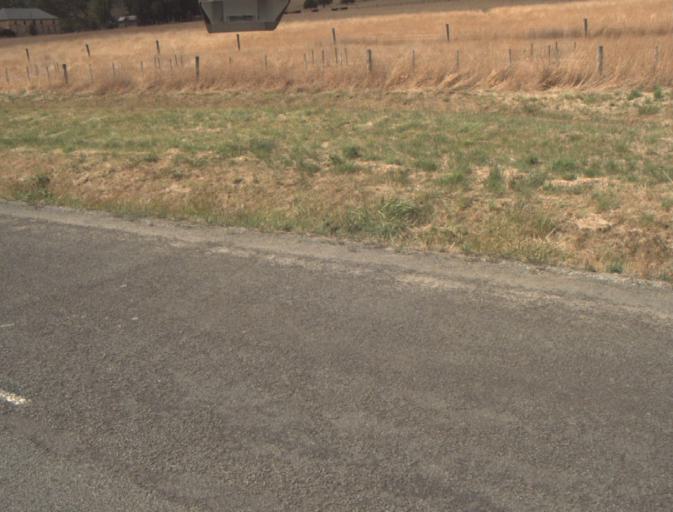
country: AU
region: Tasmania
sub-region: Launceston
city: Mayfield
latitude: -41.3100
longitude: 147.0511
